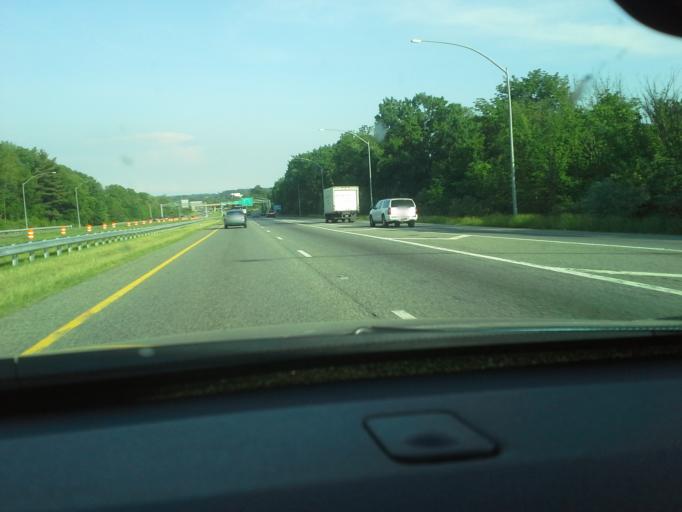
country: US
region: Maryland
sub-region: Howard County
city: West Elkridge
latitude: 39.1945
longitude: -76.7637
